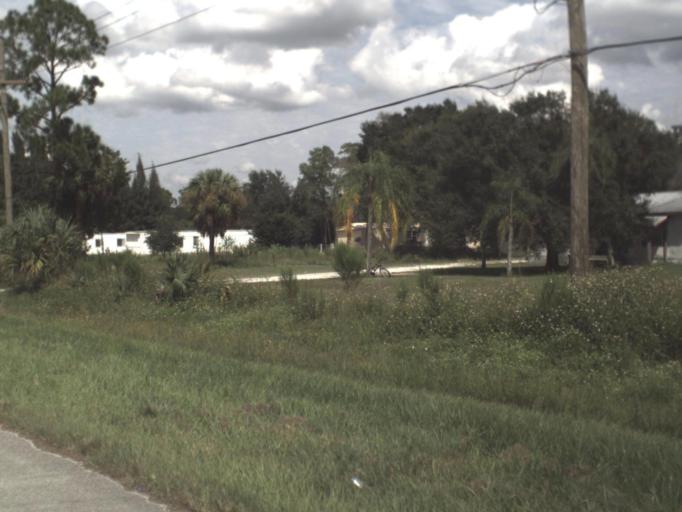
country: US
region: Florida
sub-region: Hendry County
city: LaBelle
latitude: 26.6909
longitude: -81.4369
